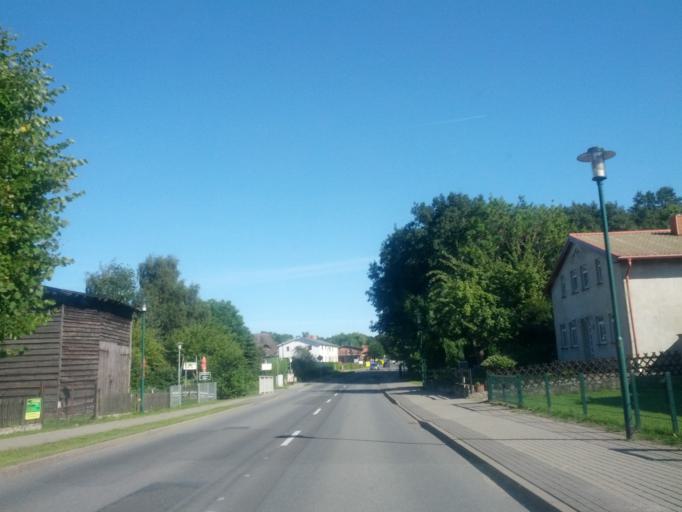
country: DE
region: Mecklenburg-Vorpommern
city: Bastorf
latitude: 54.1264
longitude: 11.6967
